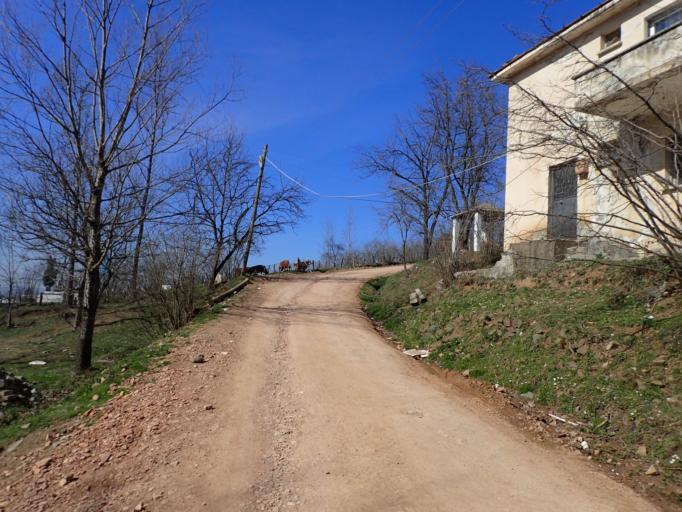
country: TR
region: Ordu
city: Catalpinar
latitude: 40.8644
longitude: 37.4975
